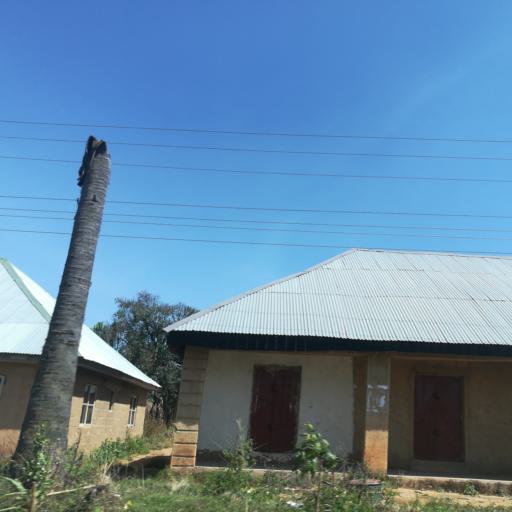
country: NG
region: Plateau
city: Bukuru
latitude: 9.7574
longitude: 8.8767
